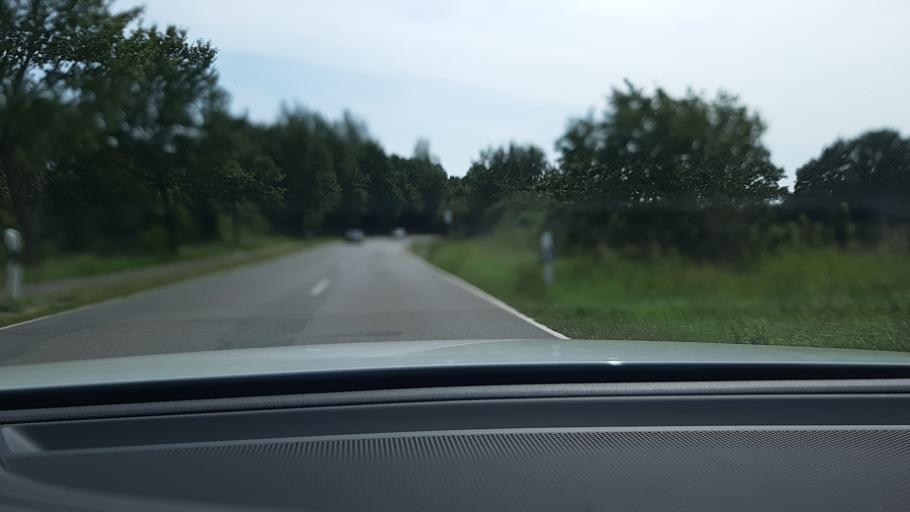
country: DE
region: Schleswig-Holstein
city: Heilshoop
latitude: 53.8818
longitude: 10.5250
